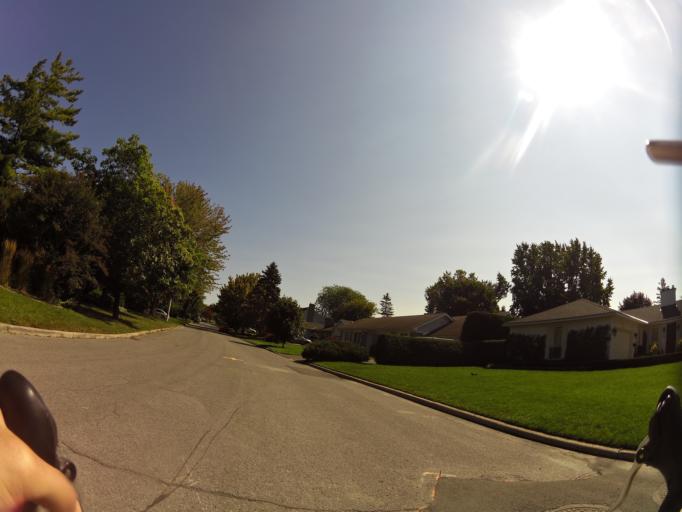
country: CA
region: Ontario
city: Ottawa
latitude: 45.3866
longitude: -75.6510
